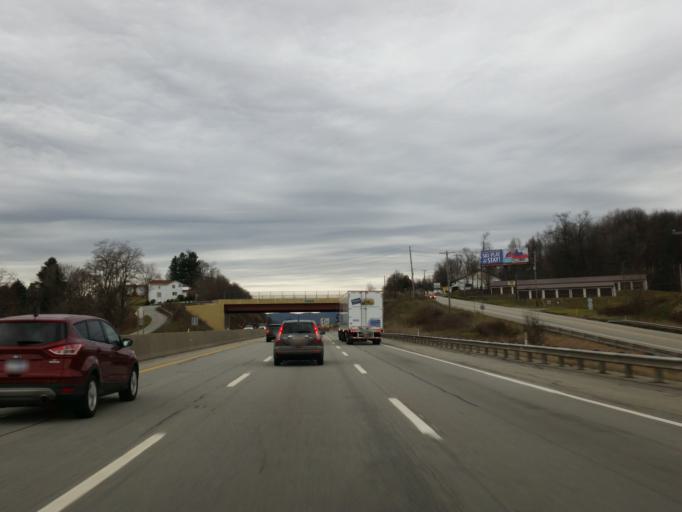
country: US
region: Pennsylvania
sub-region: Fayette County
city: Bear Rocks
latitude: 40.1140
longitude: -79.3923
